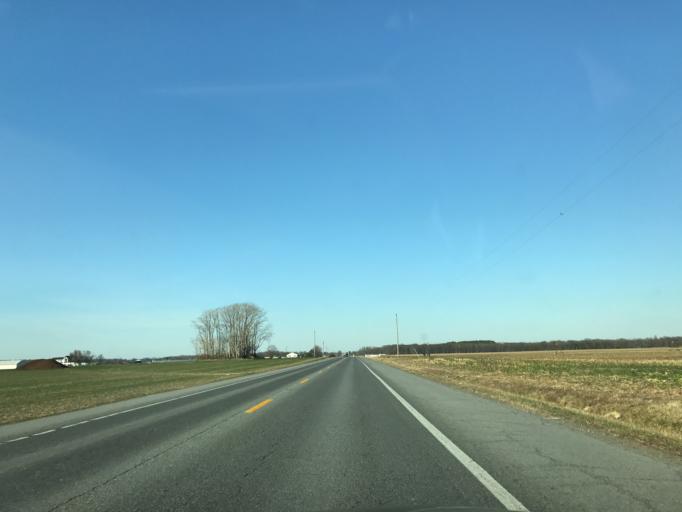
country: US
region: Maryland
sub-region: Caroline County
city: Greensboro
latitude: 39.1214
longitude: -75.8683
